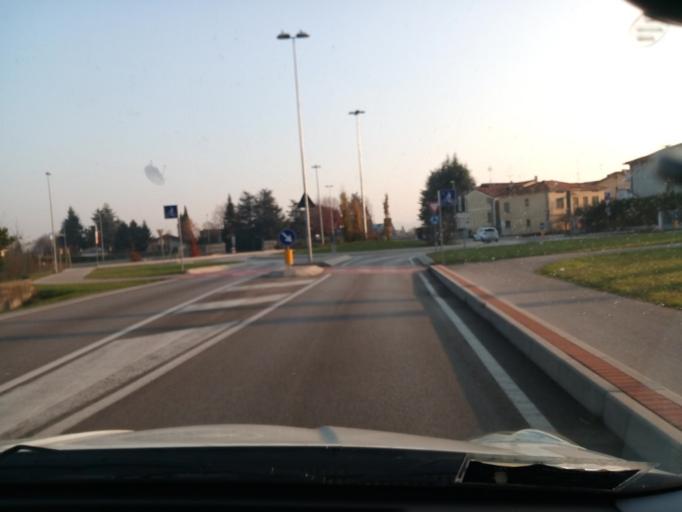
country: IT
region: Veneto
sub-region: Provincia di Vicenza
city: Schio
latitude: 45.7027
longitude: 11.3645
